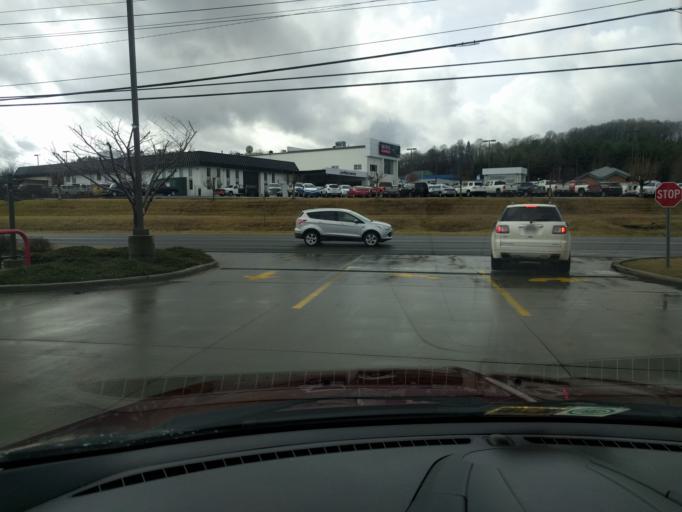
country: US
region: West Virginia
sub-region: Raleigh County
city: Beckley
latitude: 37.8046
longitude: -81.1829
